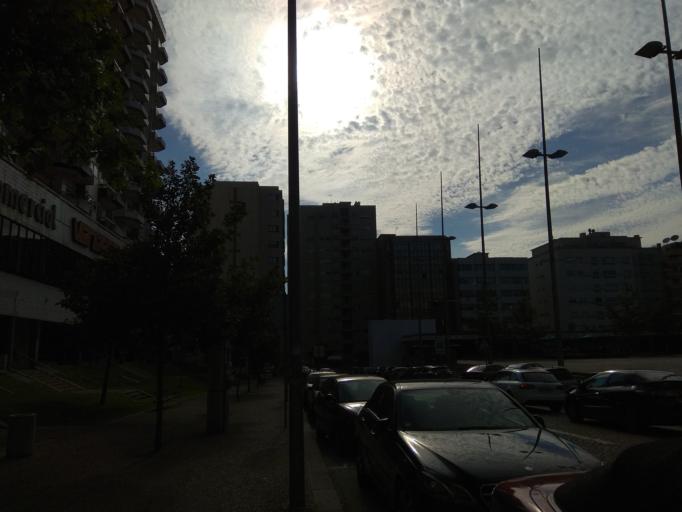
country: PT
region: Porto
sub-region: Maia
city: Maia
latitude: 41.2339
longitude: -8.6248
